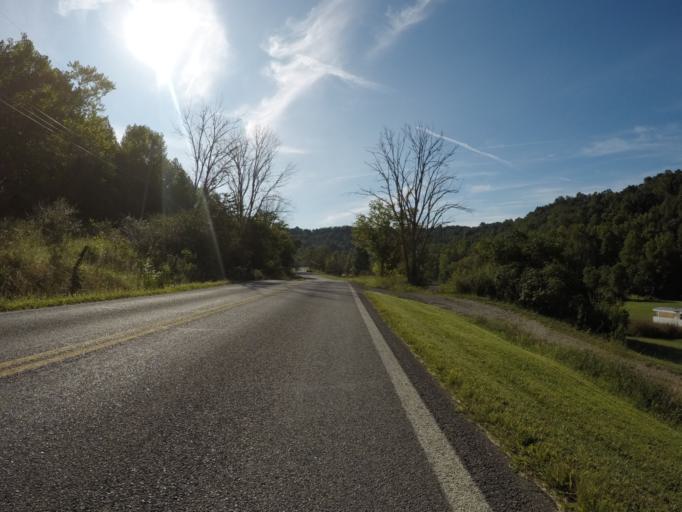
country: US
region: West Virginia
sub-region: Cabell County
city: Huntington
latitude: 38.4960
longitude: -82.5006
